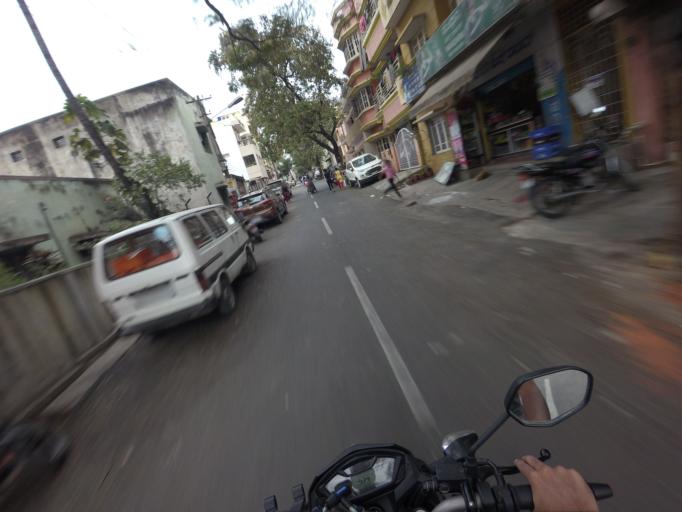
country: IN
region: Karnataka
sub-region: Bangalore Urban
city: Bangalore
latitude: 12.9675
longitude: 77.5449
